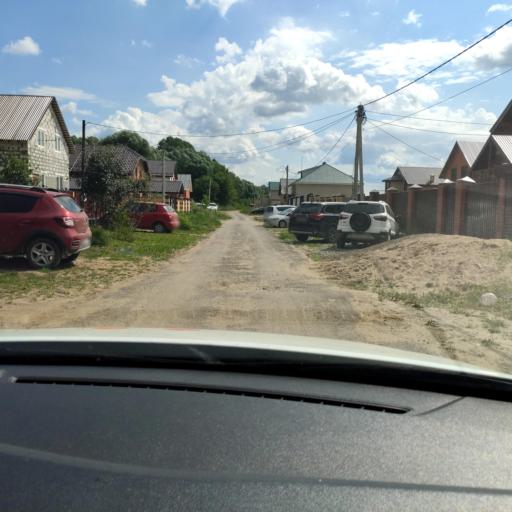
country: RU
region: Tatarstan
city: Stolbishchi
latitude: 55.7471
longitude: 49.2791
